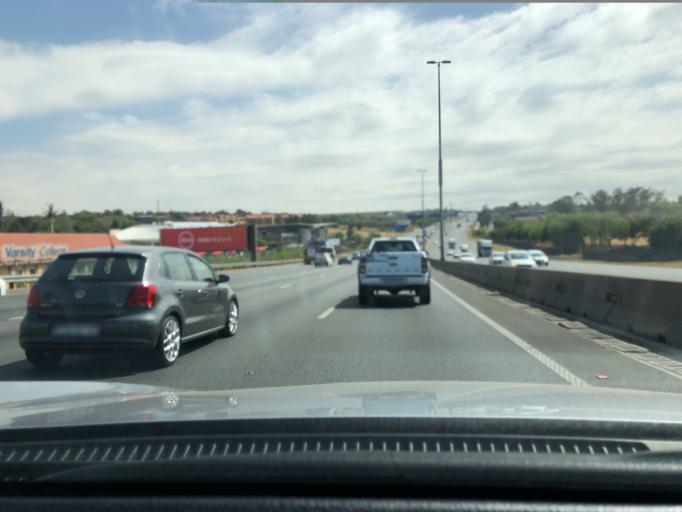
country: ZA
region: Gauteng
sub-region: City of Johannesburg Metropolitan Municipality
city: Midrand
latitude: -25.9980
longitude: 28.1213
